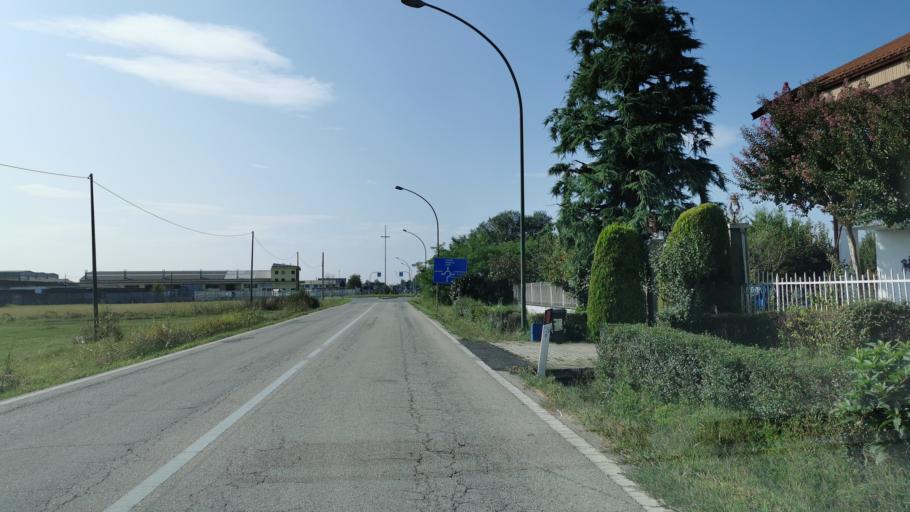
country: IT
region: Piedmont
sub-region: Provincia di Torino
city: Leini
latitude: 45.2039
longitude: 7.7268
